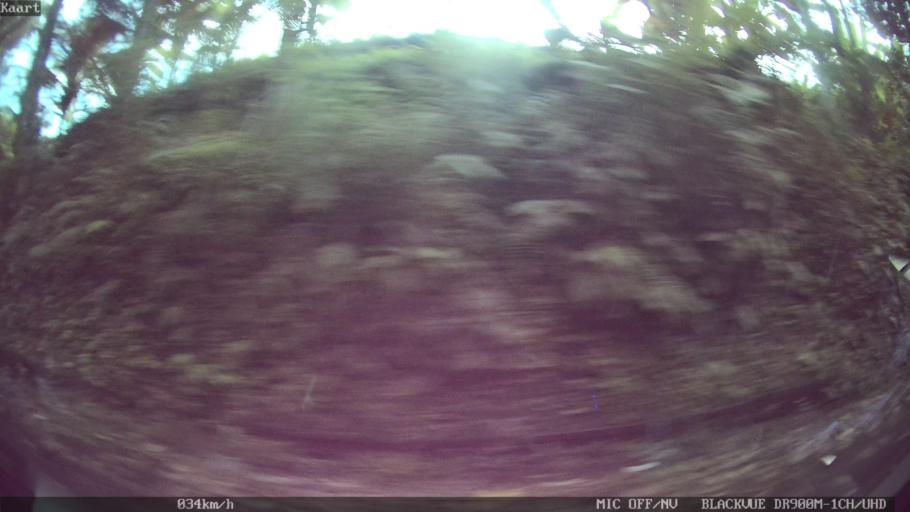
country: ID
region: Bali
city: Banjar Pesalakan
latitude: -8.5066
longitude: 115.3022
